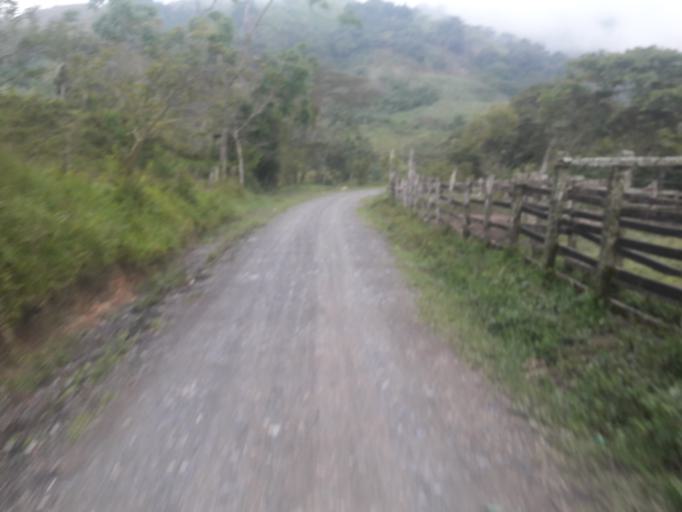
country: CO
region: Boyaca
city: Quipama
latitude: 5.5862
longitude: -74.2254
